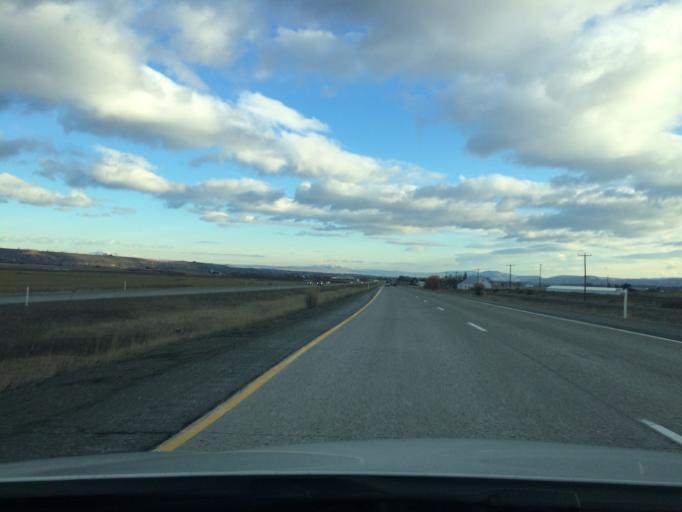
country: US
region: Washington
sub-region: Kittitas County
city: Ellensburg
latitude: 47.0752
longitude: -120.7178
